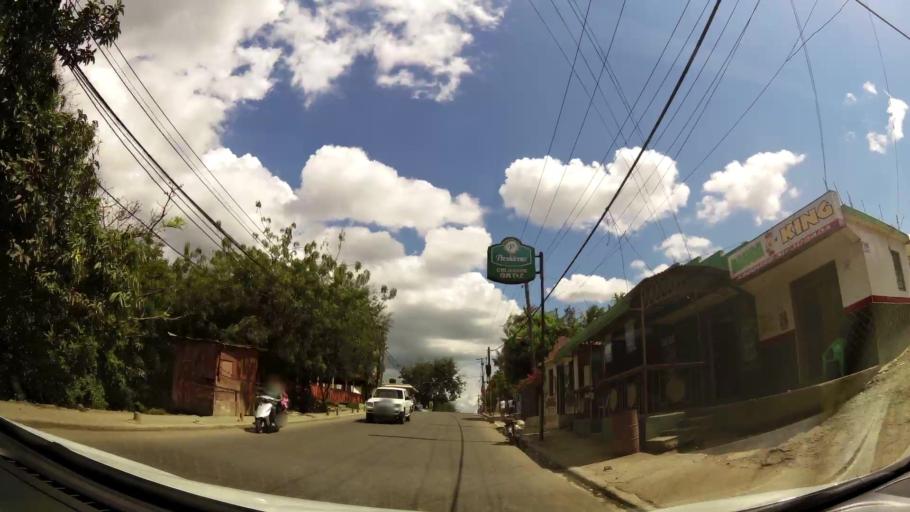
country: DO
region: Santiago
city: Santiago de los Caballeros
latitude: 19.4101
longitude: -70.6725
